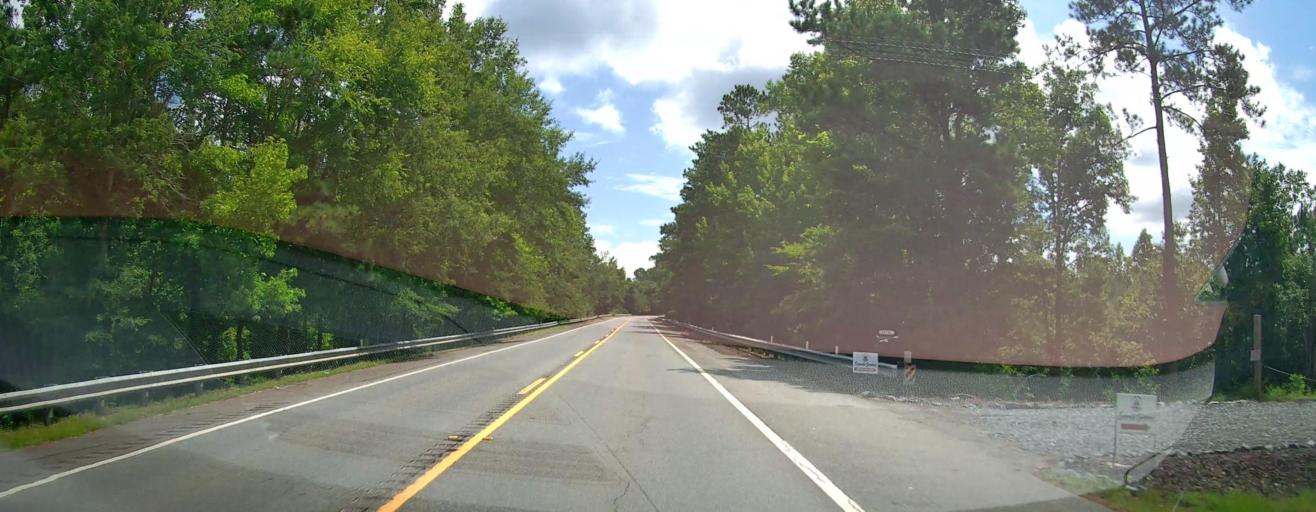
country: US
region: Georgia
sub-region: Bibb County
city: West Point
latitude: 32.8077
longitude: -83.8369
